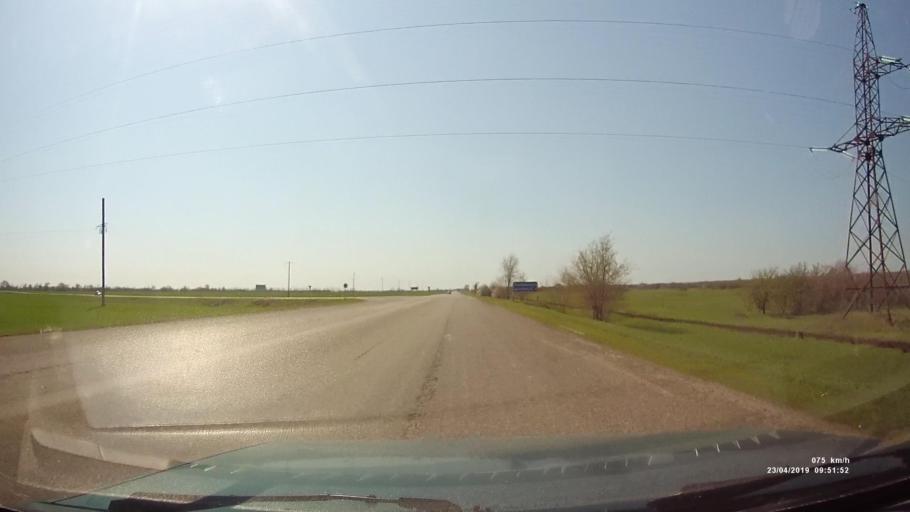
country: RU
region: Rostov
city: Orlovskiy
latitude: 46.8505
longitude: 42.0428
